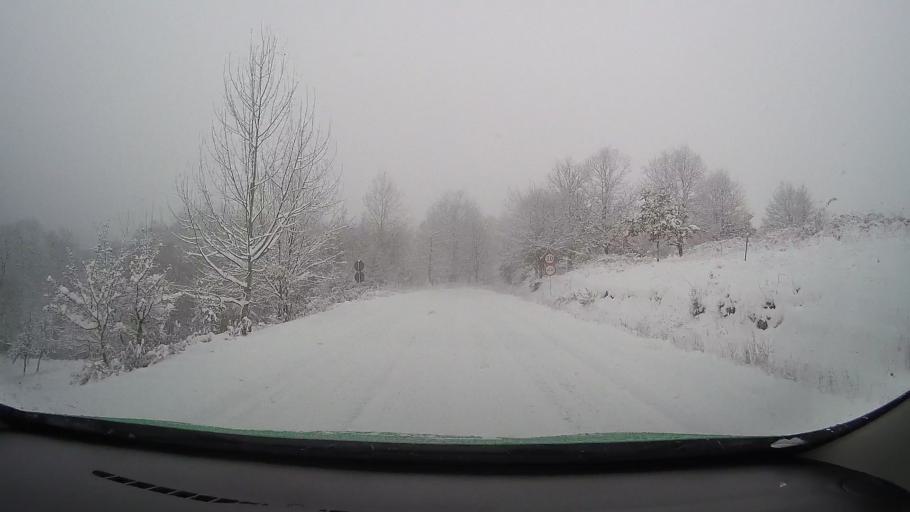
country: RO
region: Hunedoara
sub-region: Comuna Teliucu Inferior
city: Teliucu Inferior
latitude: 45.6921
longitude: 22.8929
